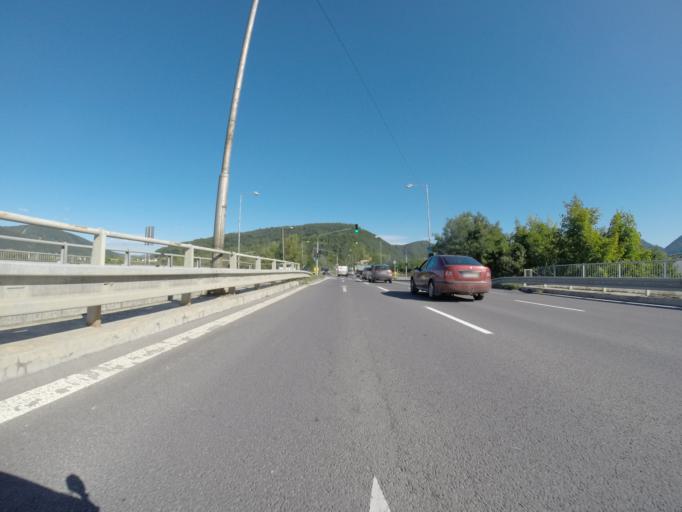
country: SK
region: Trenciansky
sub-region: Okres Povazska Bystrica
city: Povazska Bystrica
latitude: 49.1210
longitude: 18.4380
